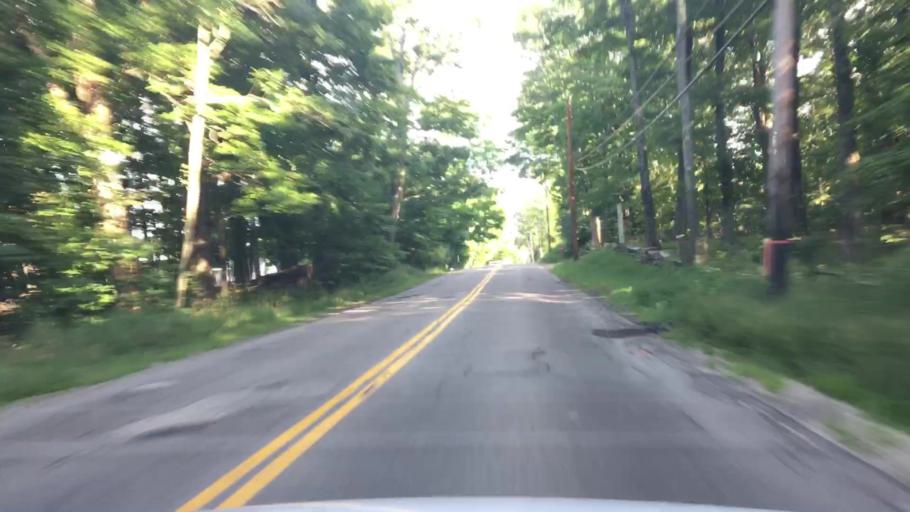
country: US
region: Maine
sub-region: Cumberland County
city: South Windham
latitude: 43.7146
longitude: -70.3903
